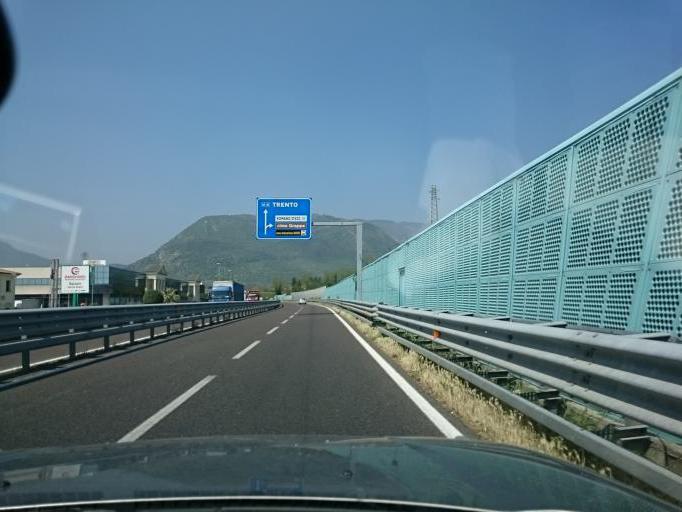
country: IT
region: Veneto
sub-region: Provincia di Vicenza
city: Romano d'Ezzelino
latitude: 45.7810
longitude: 11.7598
